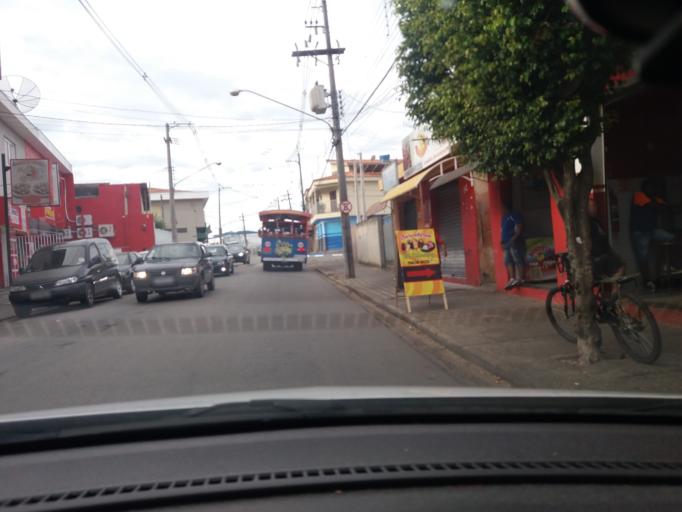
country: BR
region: Sao Paulo
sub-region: Bom Jesus Dos Perdoes
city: Bom Jesus dos Perdoes
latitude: -23.1299
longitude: -46.4669
